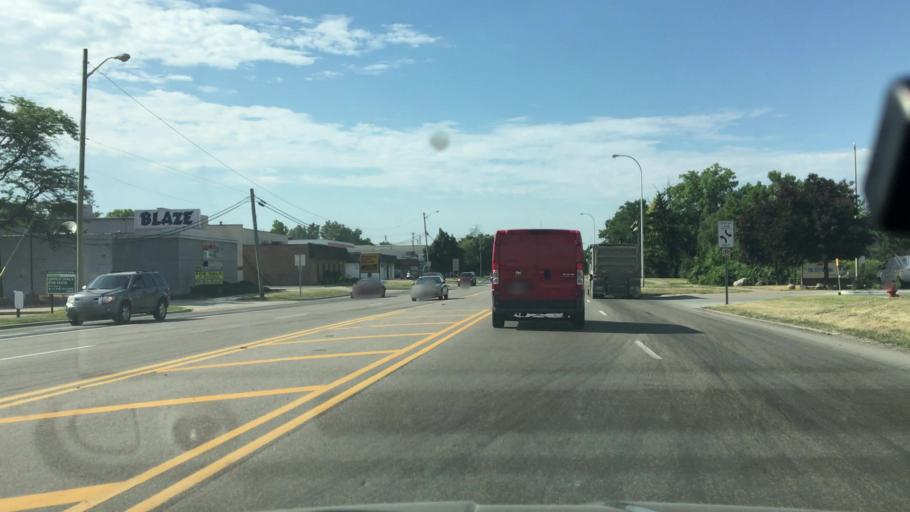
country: US
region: Michigan
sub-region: Wayne County
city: Redford
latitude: 42.3834
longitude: -83.3143
